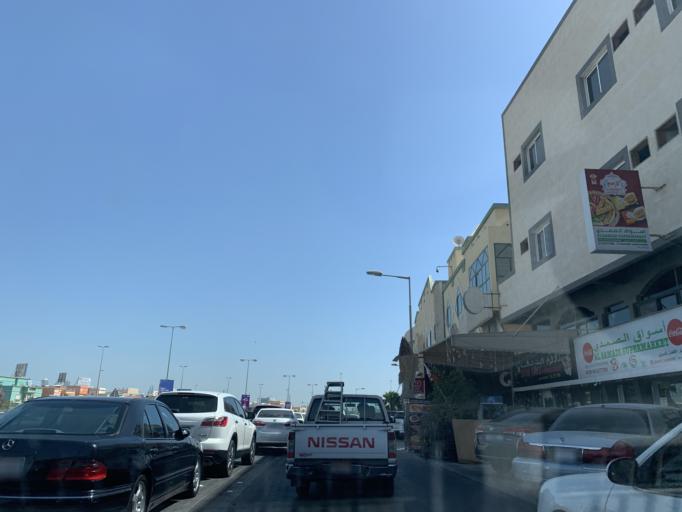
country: BH
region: Manama
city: Jidd Hafs
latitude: 26.2009
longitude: 50.5603
